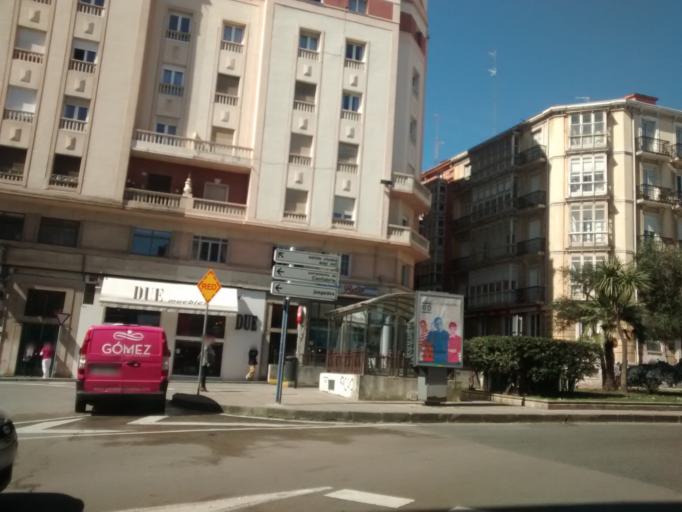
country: ES
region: Cantabria
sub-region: Provincia de Cantabria
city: Santander
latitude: 43.4614
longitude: -3.8174
